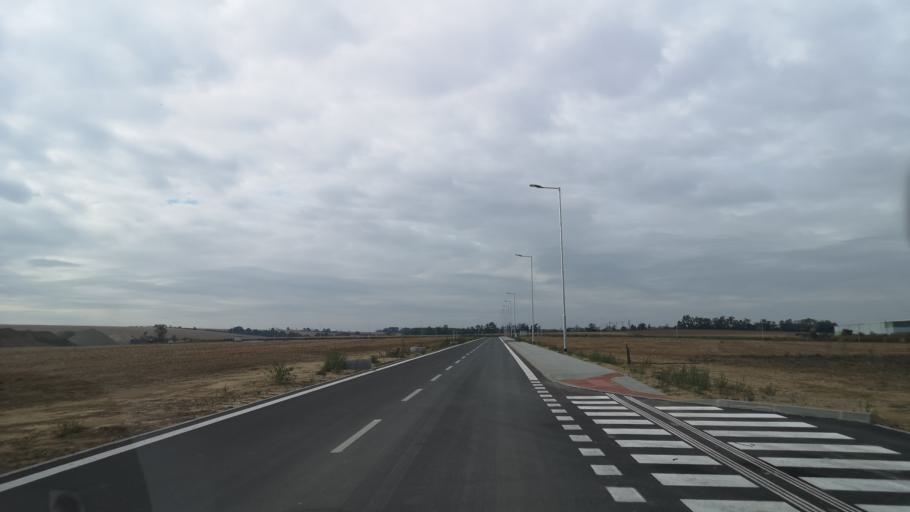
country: SK
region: Nitriansky
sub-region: Okres Nitra
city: Nitra
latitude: 48.3226
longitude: 18.0280
